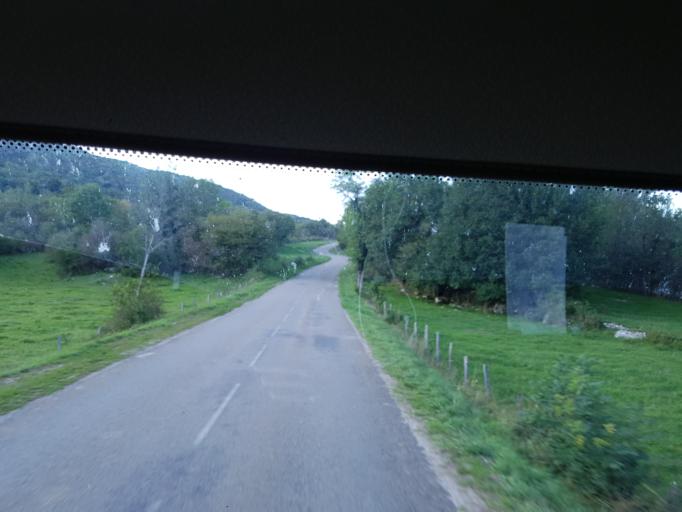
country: FR
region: Franche-Comte
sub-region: Departement du Jura
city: Moirans-en-Montagne
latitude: 46.4072
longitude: 5.6485
